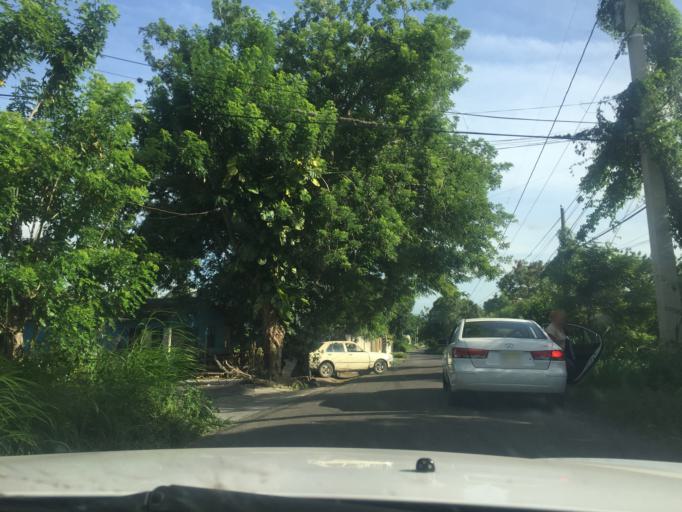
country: DO
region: Santiago
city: Tamboril
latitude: 19.4935
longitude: -70.6353
